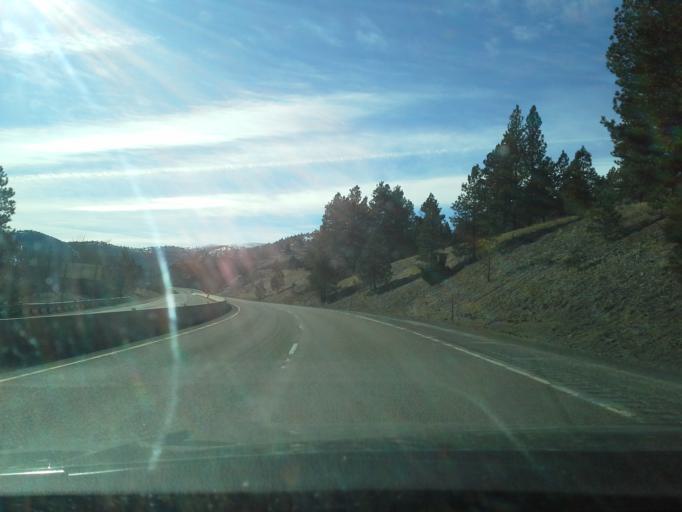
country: US
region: Montana
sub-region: Lewis and Clark County
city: Helena Valley Northwest
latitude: 46.9475
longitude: -112.1173
